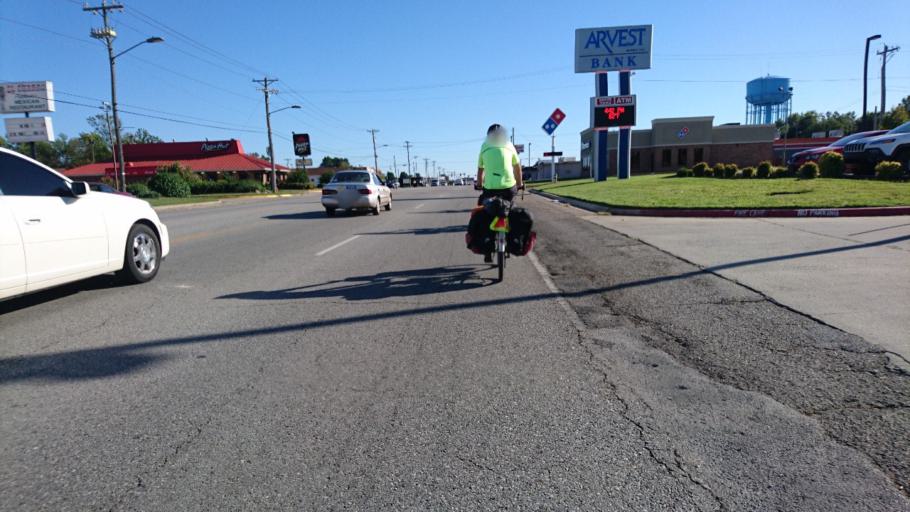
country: US
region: Oklahoma
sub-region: Ottawa County
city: Miami
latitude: 36.8914
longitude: -94.8776
